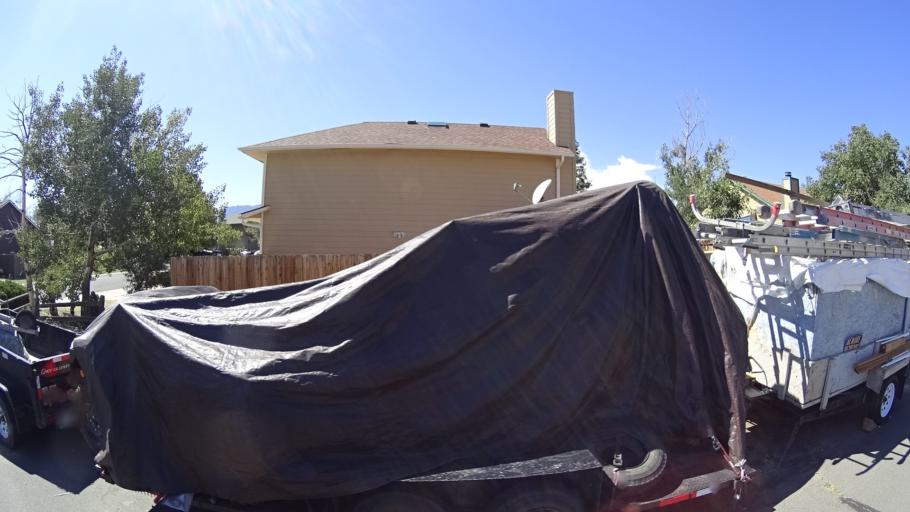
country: US
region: Colorado
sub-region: El Paso County
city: Stratmoor
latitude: 38.7826
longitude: -104.7428
